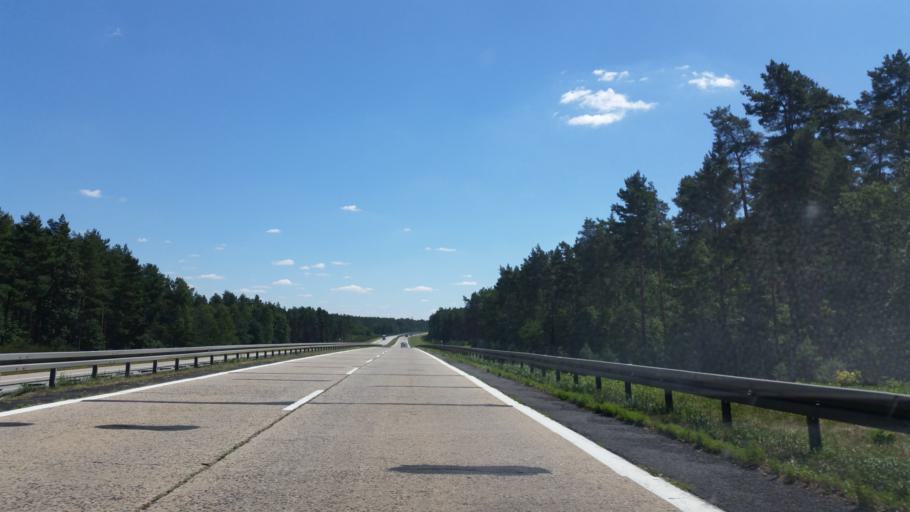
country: PL
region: Lower Silesian Voivodeship
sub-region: Powiat boleslawiecki
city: Boleslawiec
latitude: 51.4039
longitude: 15.5124
